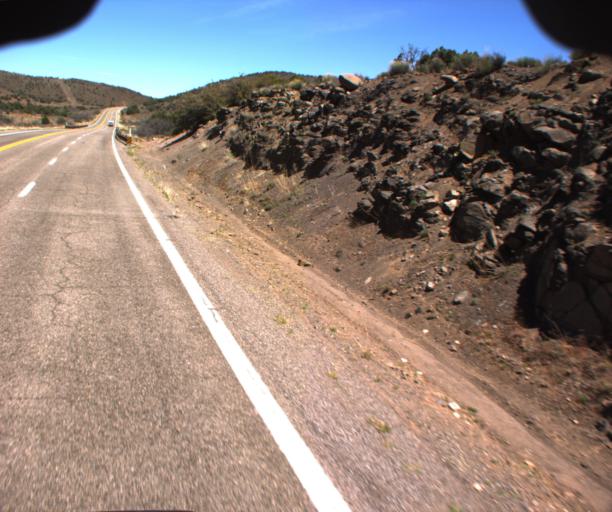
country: US
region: Arizona
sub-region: Mohave County
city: Peach Springs
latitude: 35.4344
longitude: -113.6481
